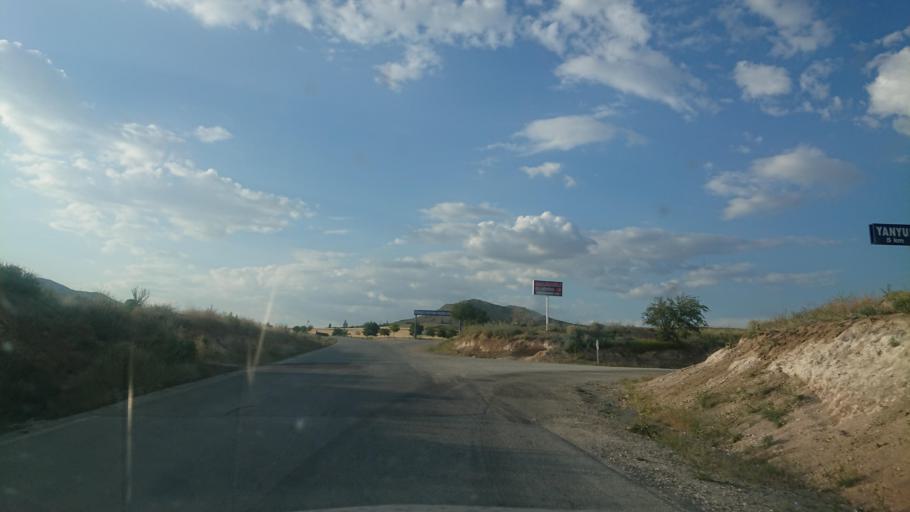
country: TR
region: Aksaray
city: Balci
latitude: 38.5780
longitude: 34.1056
